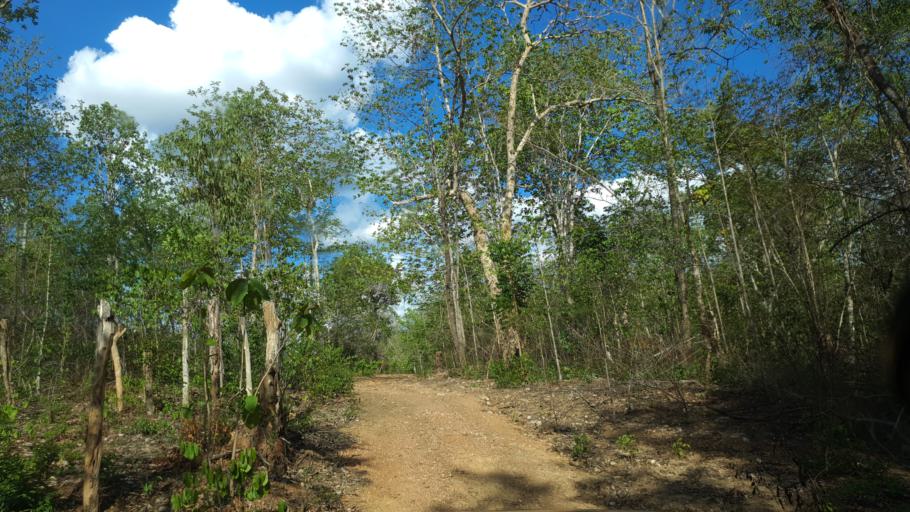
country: TH
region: Lampang
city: Sop Prap
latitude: 17.8412
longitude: 99.2872
